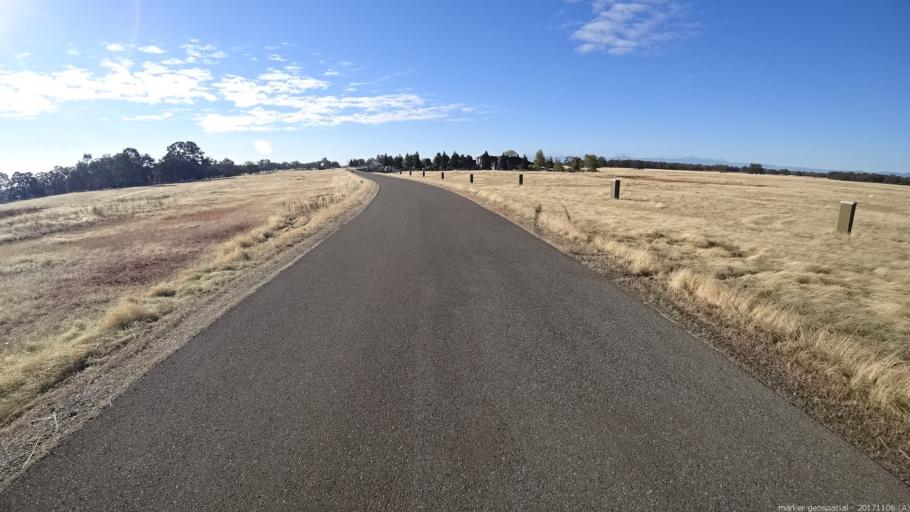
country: US
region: California
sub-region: Shasta County
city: Palo Cedro
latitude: 40.4985
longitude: -122.2459
